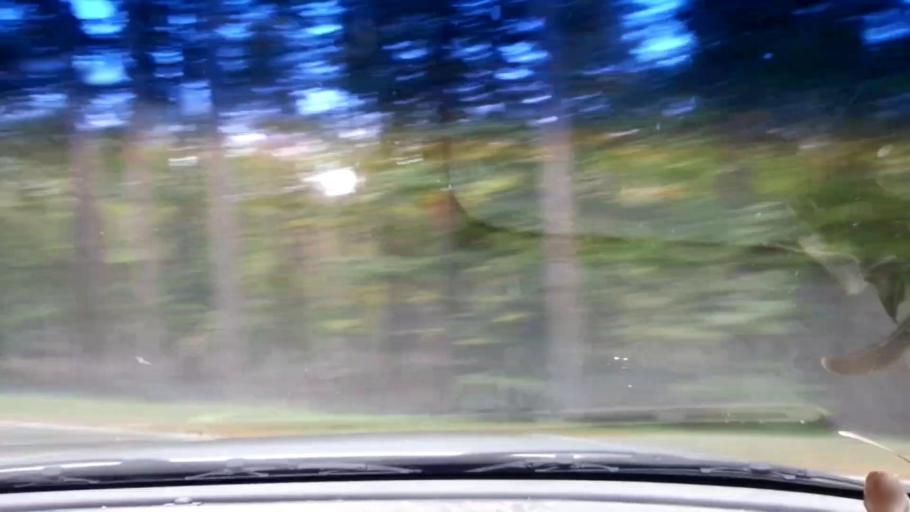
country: DE
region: Bavaria
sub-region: Upper Franconia
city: Priesendorf
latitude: 49.9201
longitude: 10.7174
